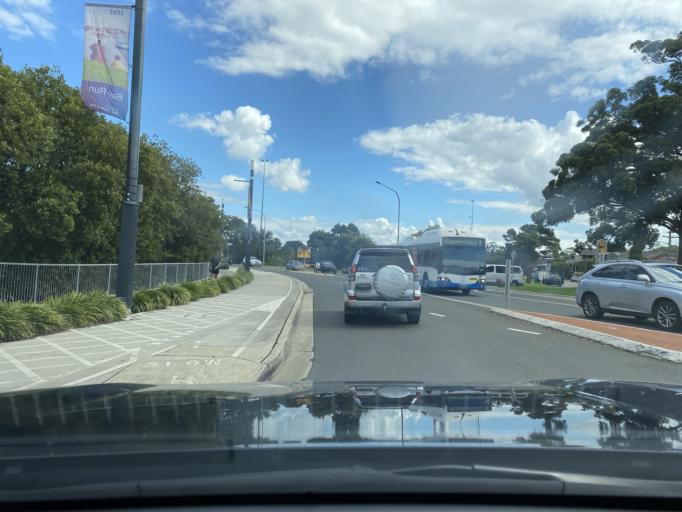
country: AU
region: New South Wales
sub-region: Canada Bay
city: Wareemba
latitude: -33.8682
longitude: 151.1417
